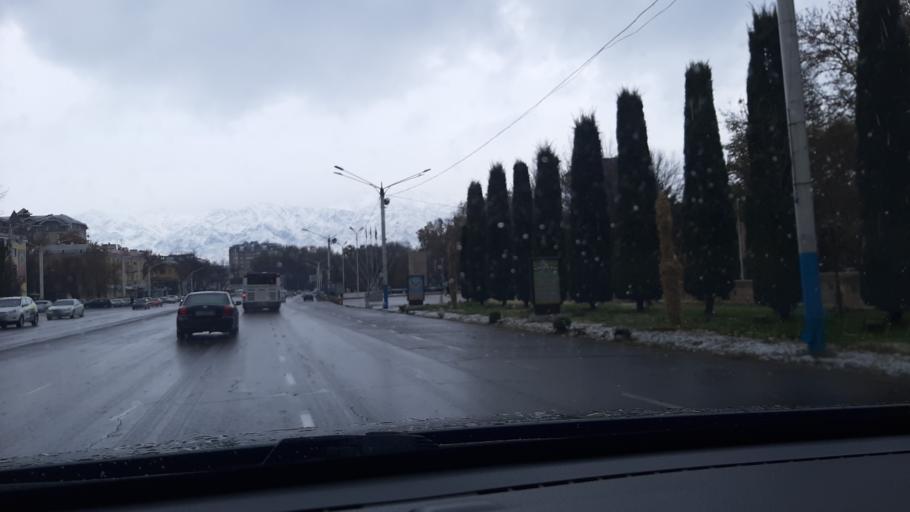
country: TJ
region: Viloyati Sughd
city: Khujand
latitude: 40.2828
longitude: 69.6241
